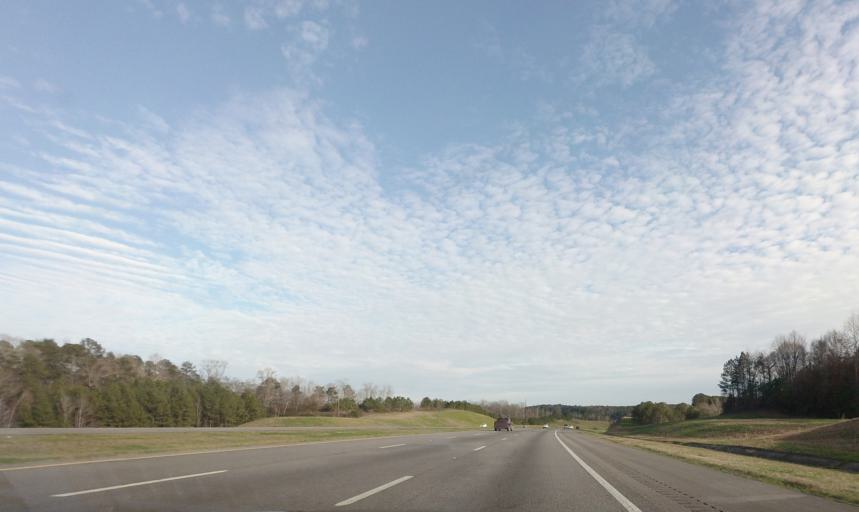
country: US
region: Alabama
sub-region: Walker County
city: Cordova
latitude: 33.7130
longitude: -87.1527
